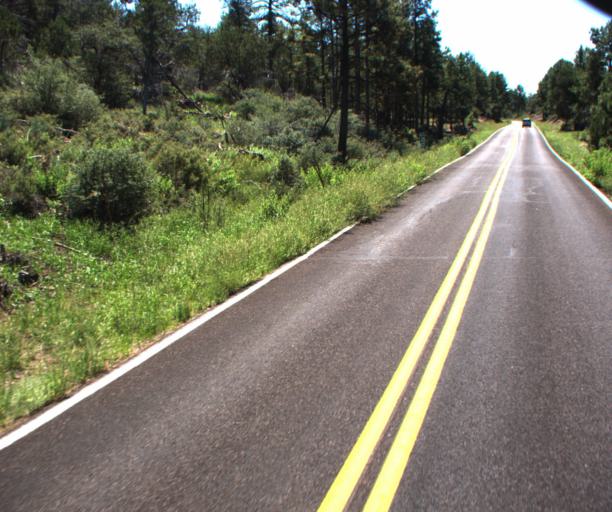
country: US
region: Arizona
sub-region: Greenlee County
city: Morenci
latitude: 33.4202
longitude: -109.3723
